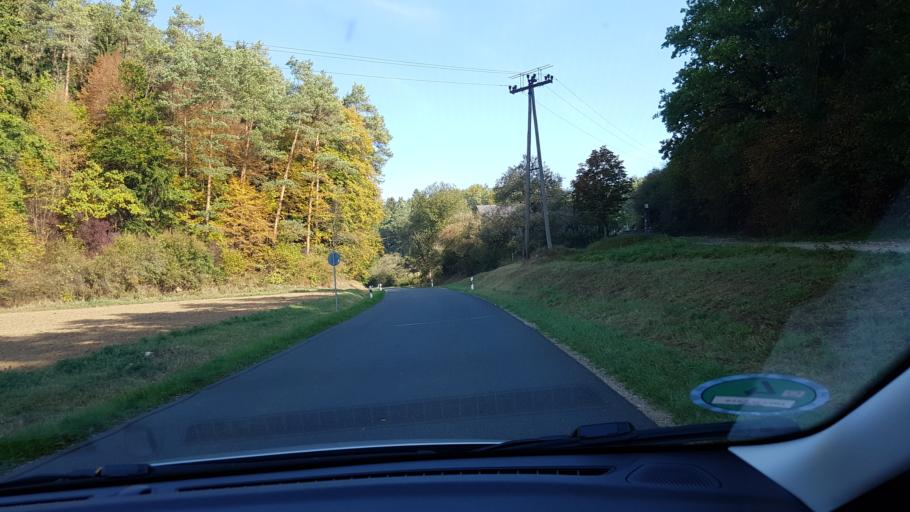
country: DE
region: Bavaria
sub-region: Upper Franconia
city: Waischenfeld
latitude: 49.8163
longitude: 11.3547
